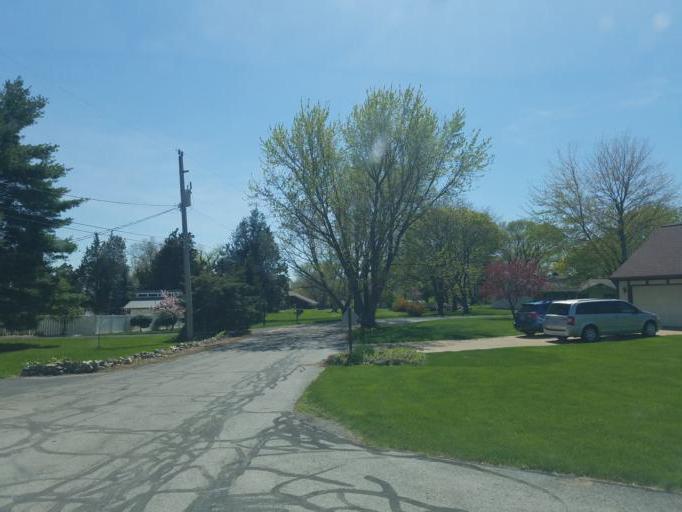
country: US
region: Ohio
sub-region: Ottawa County
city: Port Clinton
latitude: 41.5299
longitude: -82.8592
